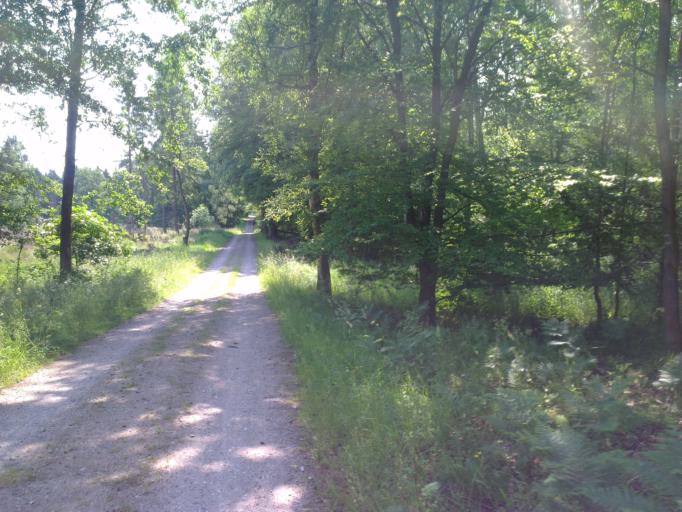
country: DK
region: Capital Region
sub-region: Allerod Kommune
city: Lillerod
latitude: 55.9175
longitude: 12.3522
